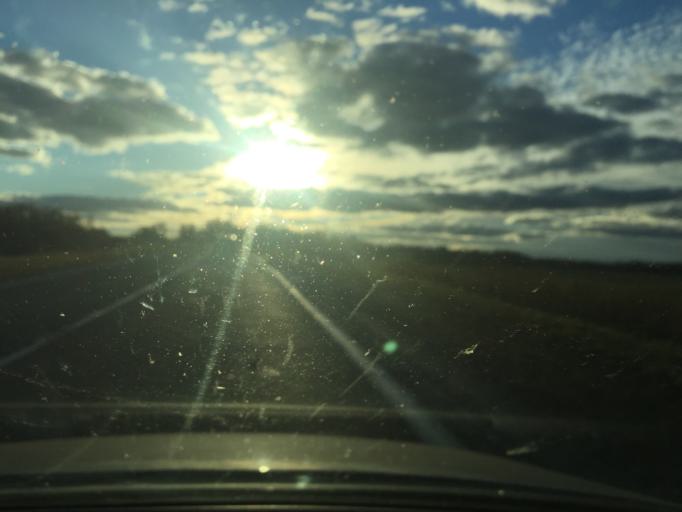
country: BY
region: Vitebsk
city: Vyerkhnyadzvinsk
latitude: 55.8351
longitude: 27.8264
